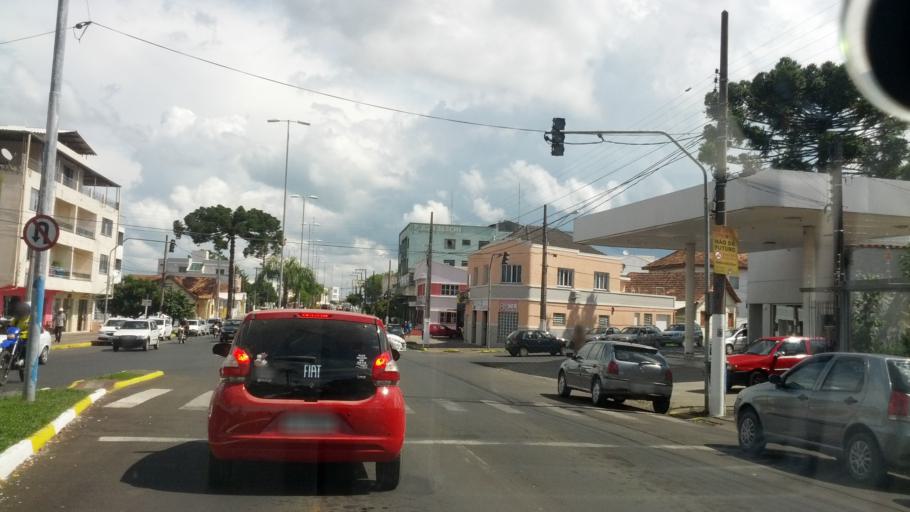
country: BR
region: Santa Catarina
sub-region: Lages
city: Lages
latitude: -27.8211
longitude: -50.3329
